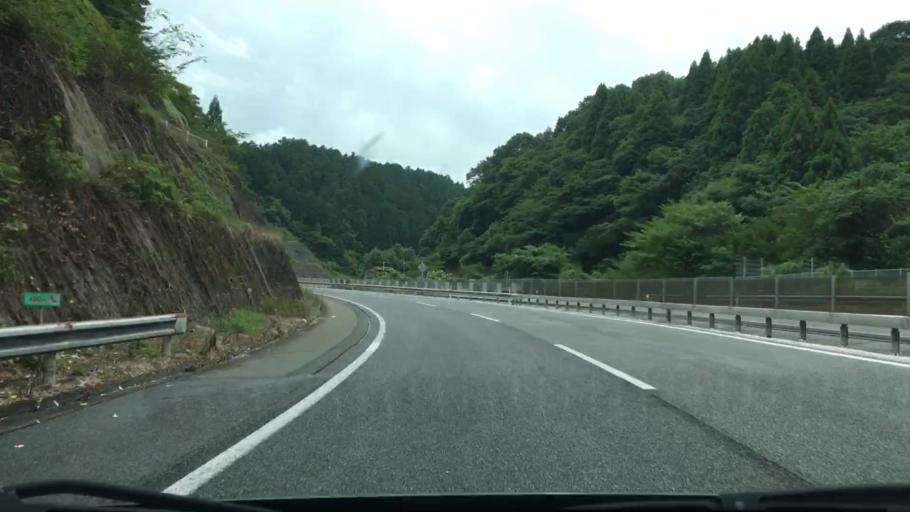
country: JP
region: Hiroshima
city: Shobara
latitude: 34.8947
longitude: 133.2258
